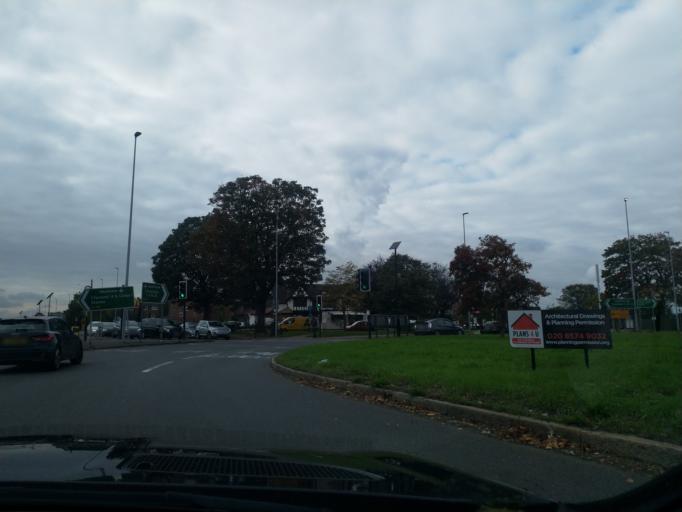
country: GB
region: England
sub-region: Greater London
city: Feltham
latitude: 51.4754
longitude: -0.3954
